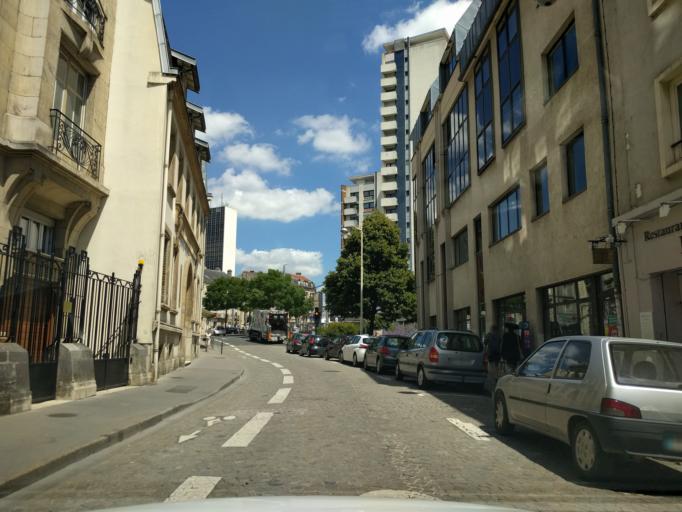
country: FR
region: Lorraine
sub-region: Departement de Meurthe-et-Moselle
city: Nancy
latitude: 48.6876
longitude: 6.1729
